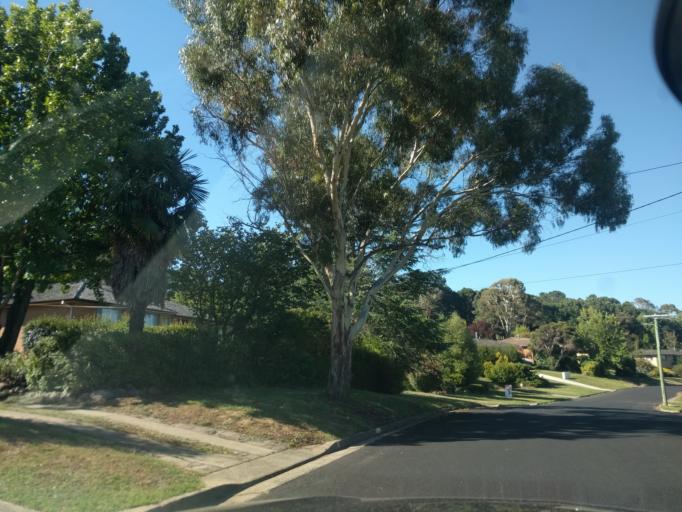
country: AU
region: New South Wales
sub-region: Armidale Dumaresq
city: Armidale
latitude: -30.5010
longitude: 151.6673
